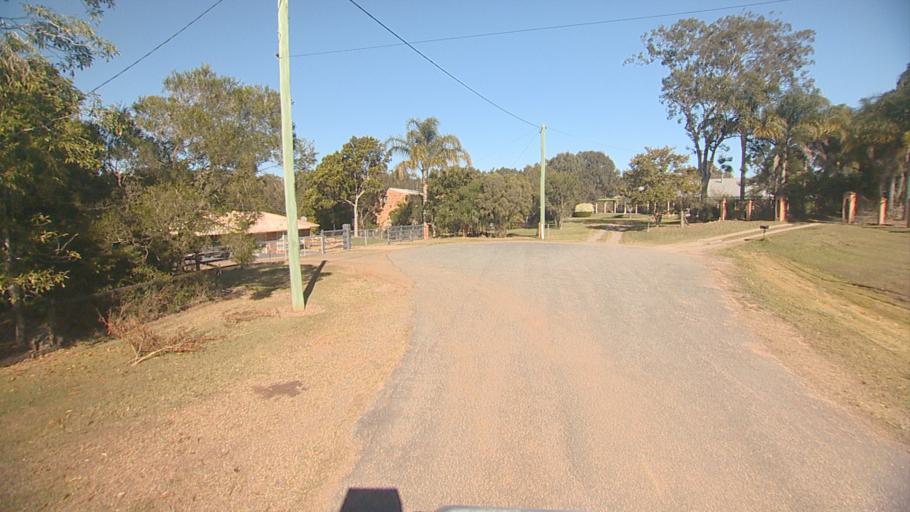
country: AU
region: Queensland
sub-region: Logan
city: Chambers Flat
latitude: -27.7619
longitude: 153.0942
